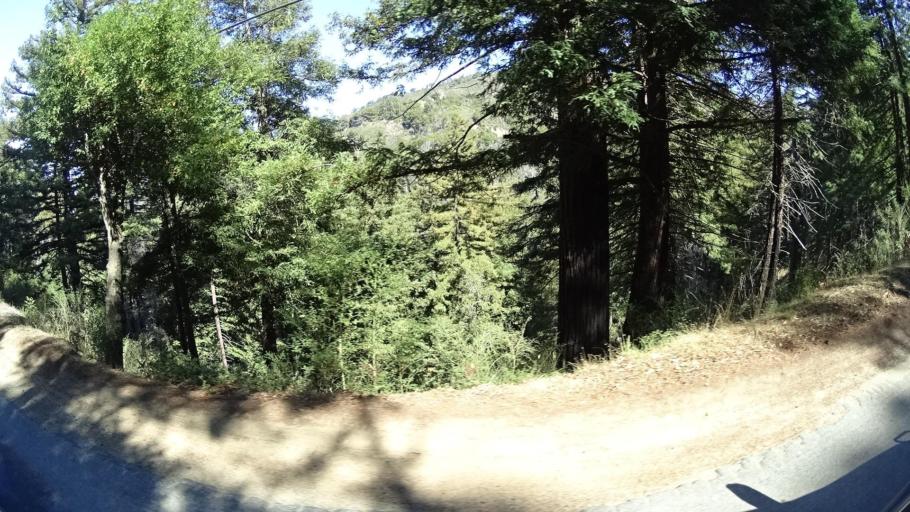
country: US
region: California
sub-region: Monterey County
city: Carmel Valley Village
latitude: 36.3762
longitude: -121.8559
